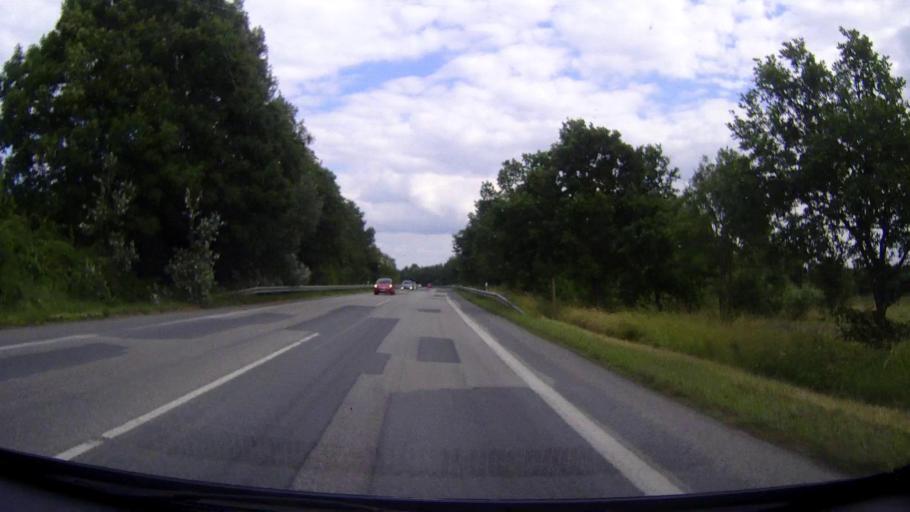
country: DE
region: Schleswig-Holstein
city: Badendorf
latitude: 53.8963
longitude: 10.5959
